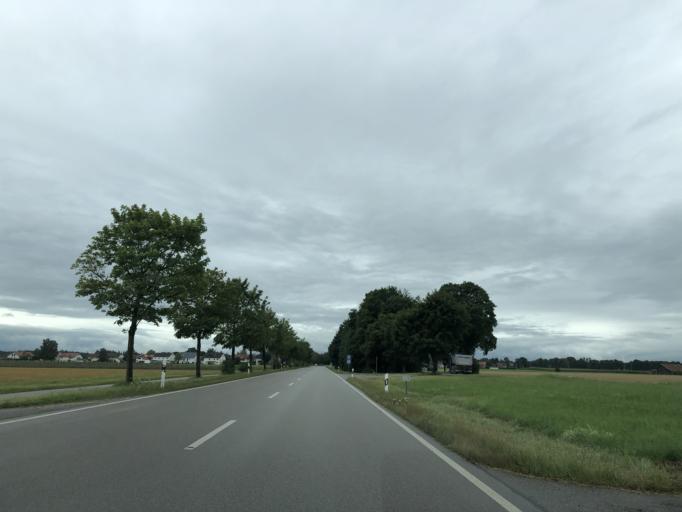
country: DE
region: Bavaria
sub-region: Upper Bavaria
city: Sauerlach
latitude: 47.9850
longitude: 11.6475
